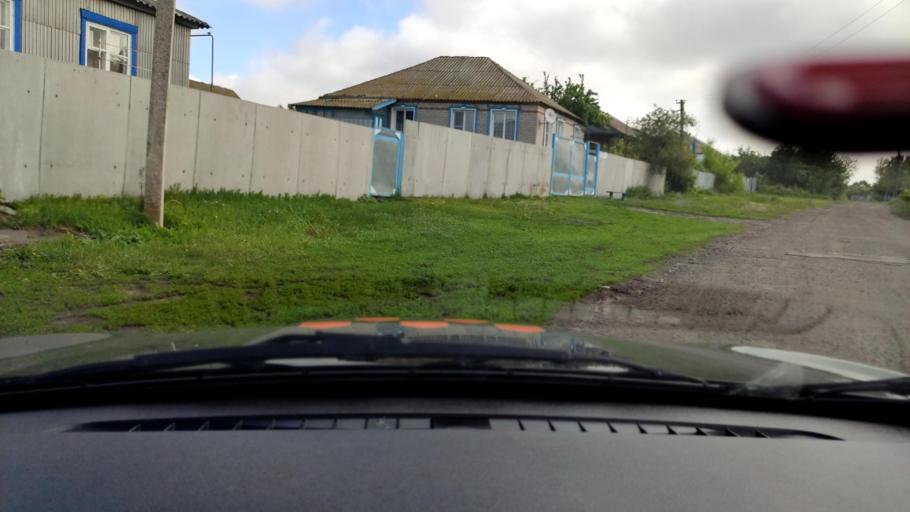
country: RU
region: Voronezj
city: Uryv-Pokrovka
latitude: 51.1101
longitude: 39.1717
